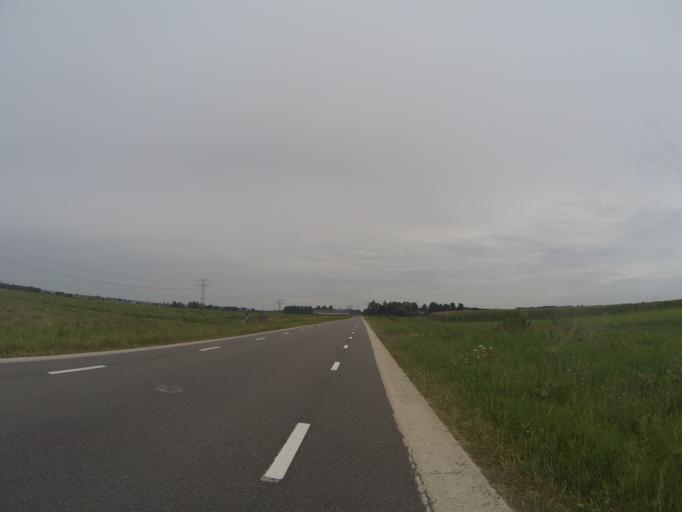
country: NL
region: Utrecht
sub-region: Gemeente Bunschoten
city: Bunschoten
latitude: 52.2409
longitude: 5.3930
